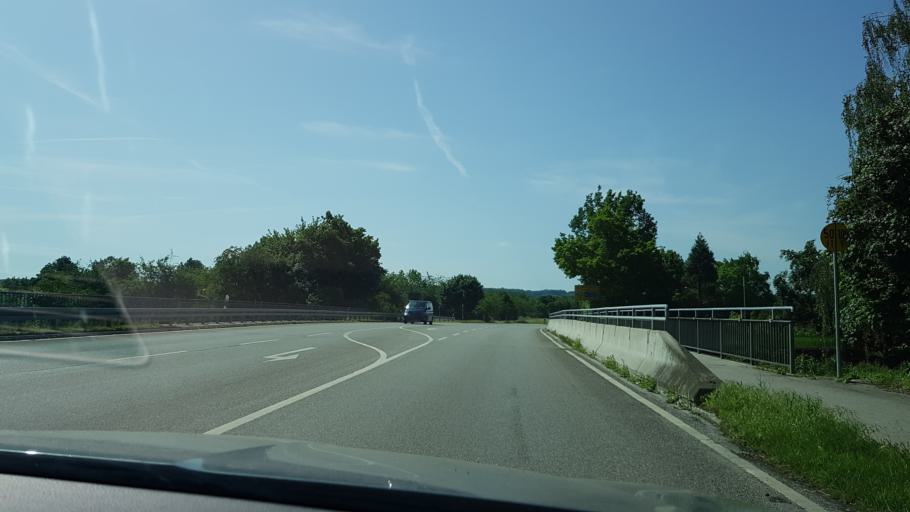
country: DE
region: Bavaria
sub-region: Upper Bavaria
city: Fuerstenfeldbruck
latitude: 48.1900
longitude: 11.2658
